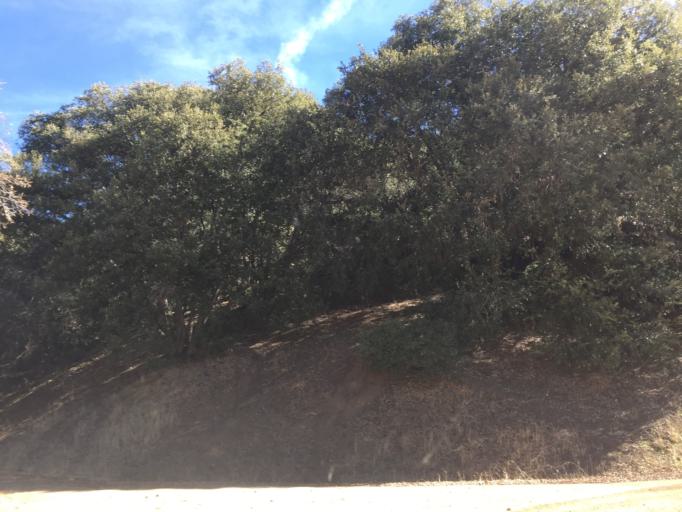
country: US
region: California
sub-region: Kern County
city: Stallion Springs
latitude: 34.9166
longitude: -118.6826
